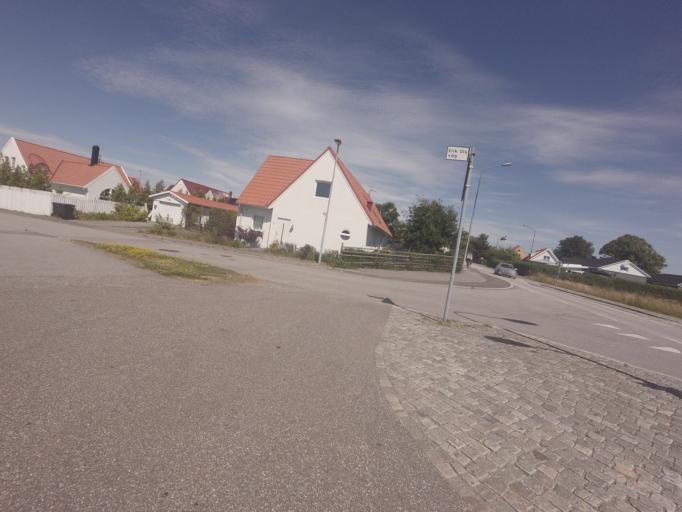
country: SE
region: Skane
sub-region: Malmo
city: Tygelsjo
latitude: 55.5255
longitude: 12.9962
